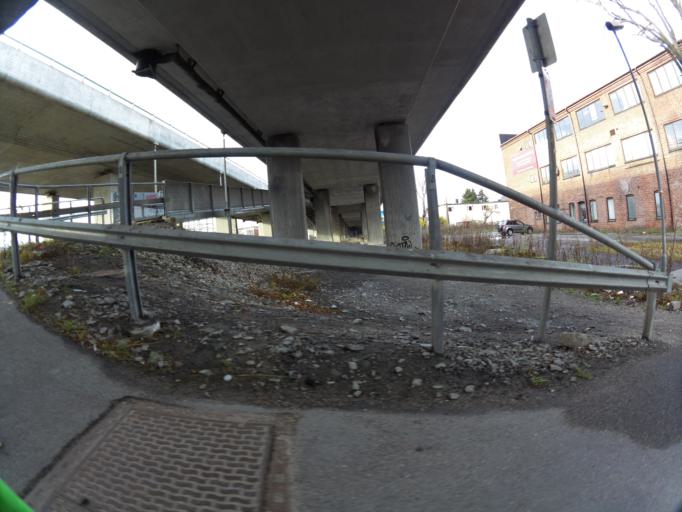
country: NO
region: Ostfold
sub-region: Sarpsborg
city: Sarpsborg
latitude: 59.2751
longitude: 11.0900
